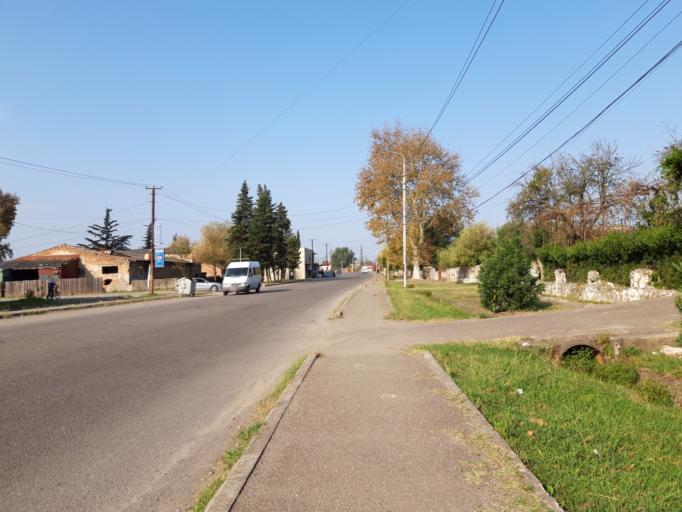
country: GE
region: Imereti
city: Samtredia
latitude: 42.1590
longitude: 42.3294
